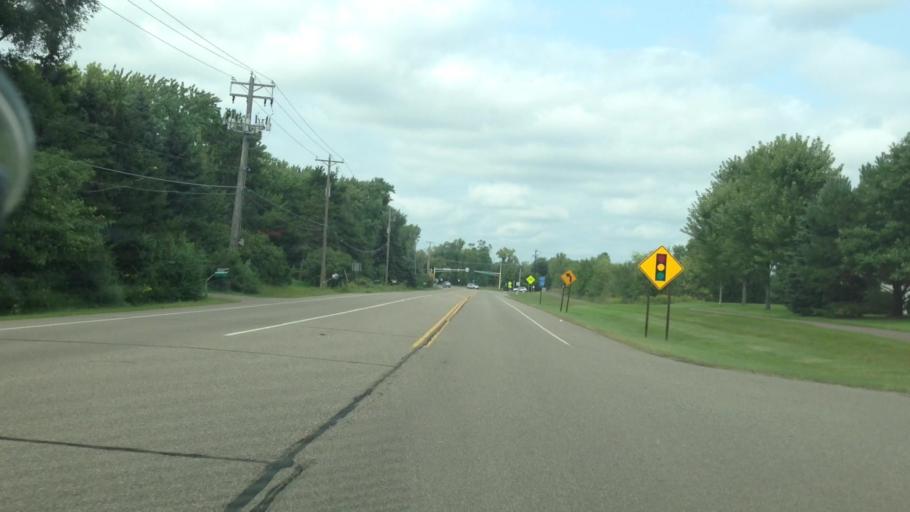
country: US
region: Minnesota
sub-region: Anoka County
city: Circle Pines
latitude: 45.1394
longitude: -93.1267
